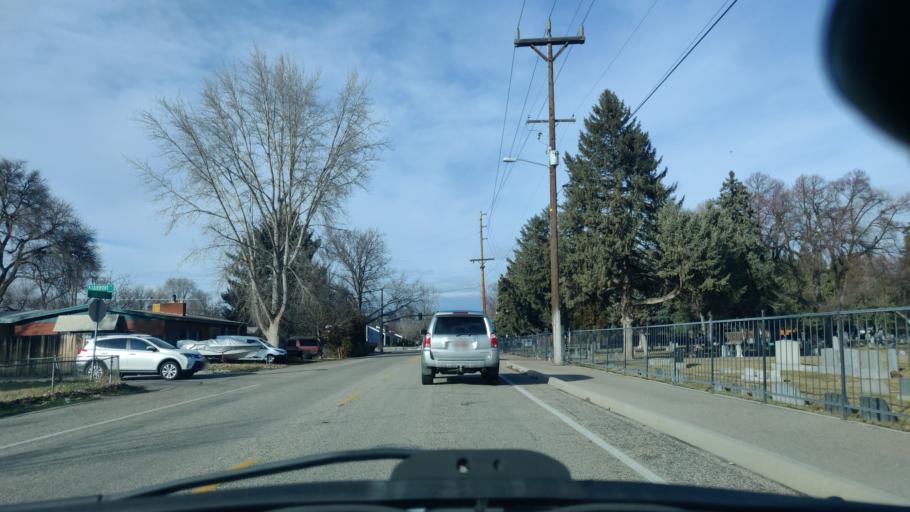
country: US
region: Idaho
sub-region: Ada County
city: Garden City
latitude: 43.6104
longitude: -116.2335
